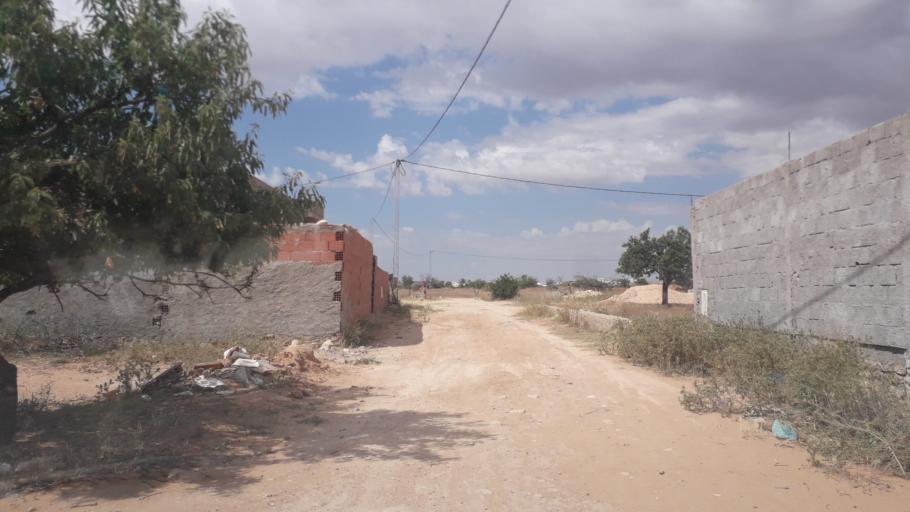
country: TN
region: Safaqis
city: Al Qarmadah
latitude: 34.8380
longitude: 10.7733
